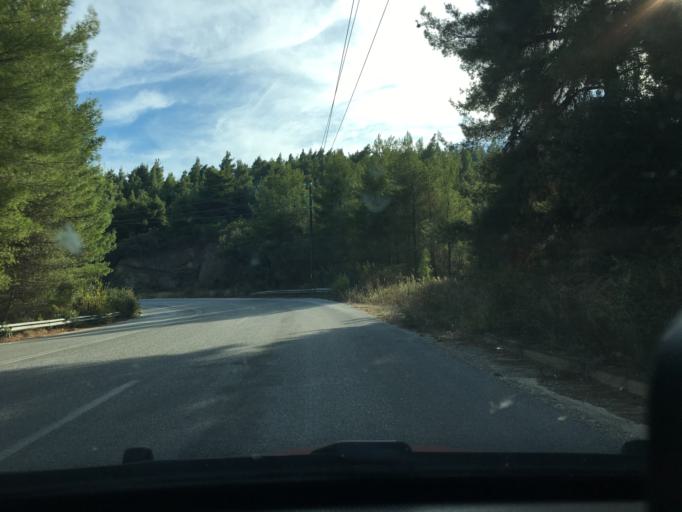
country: GR
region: Central Macedonia
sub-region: Nomos Chalkidikis
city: Agios Nikolaos
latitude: 40.2847
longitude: 23.6826
